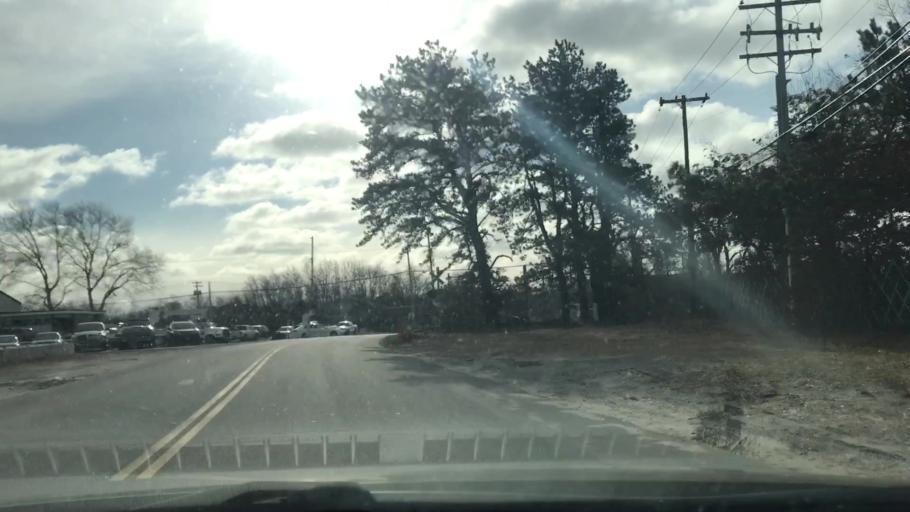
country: US
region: New York
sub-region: Suffolk County
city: Calverton
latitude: 40.9170
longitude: -72.7068
